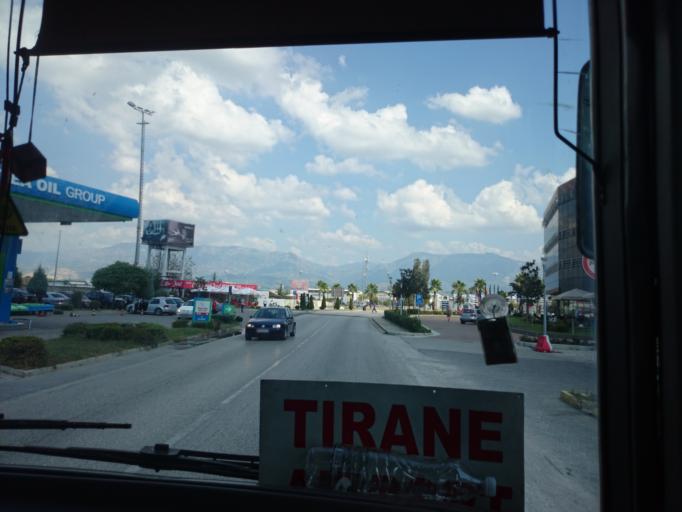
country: AL
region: Tirane
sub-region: Rrethi i Tiranes
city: Preze
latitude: 41.4206
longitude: 19.7112
